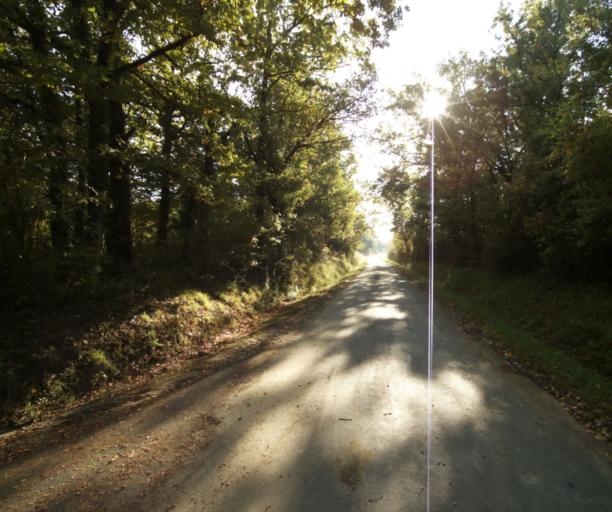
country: FR
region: Midi-Pyrenees
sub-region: Departement du Tarn-et-Garonne
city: Nohic
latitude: 43.9216
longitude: 1.4434
